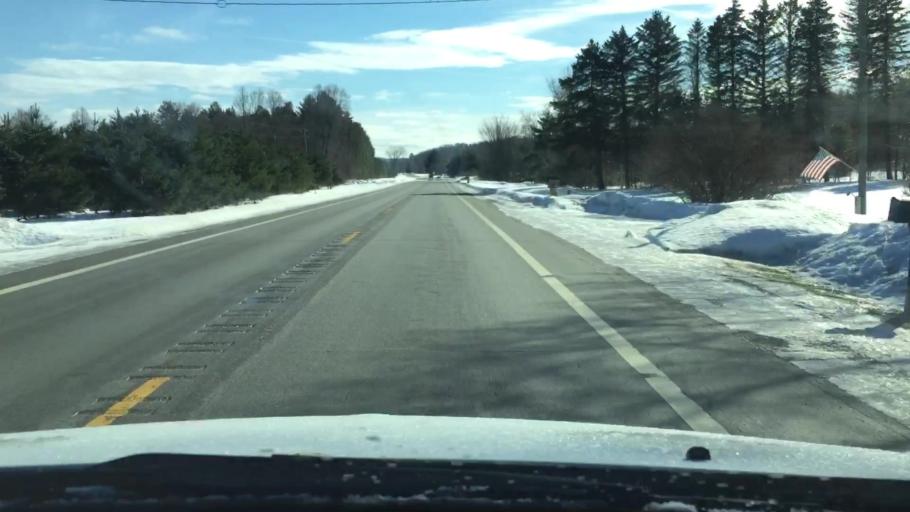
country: US
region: Michigan
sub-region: Charlevoix County
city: East Jordan
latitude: 45.0781
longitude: -85.0883
